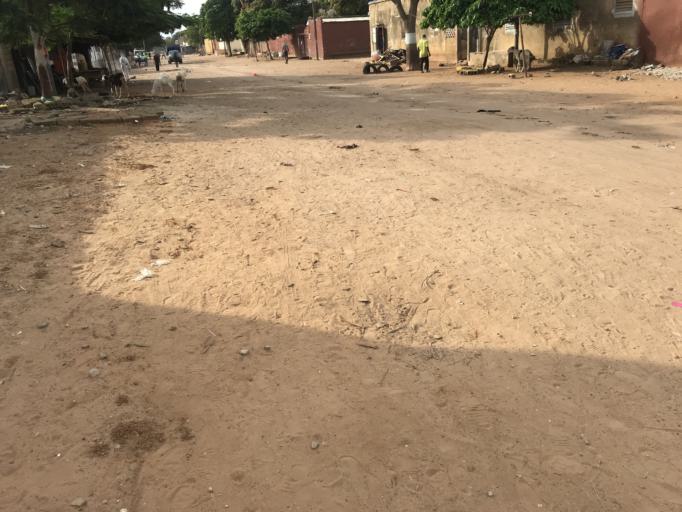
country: SN
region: Thies
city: Warang
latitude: 14.4181
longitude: -16.9608
